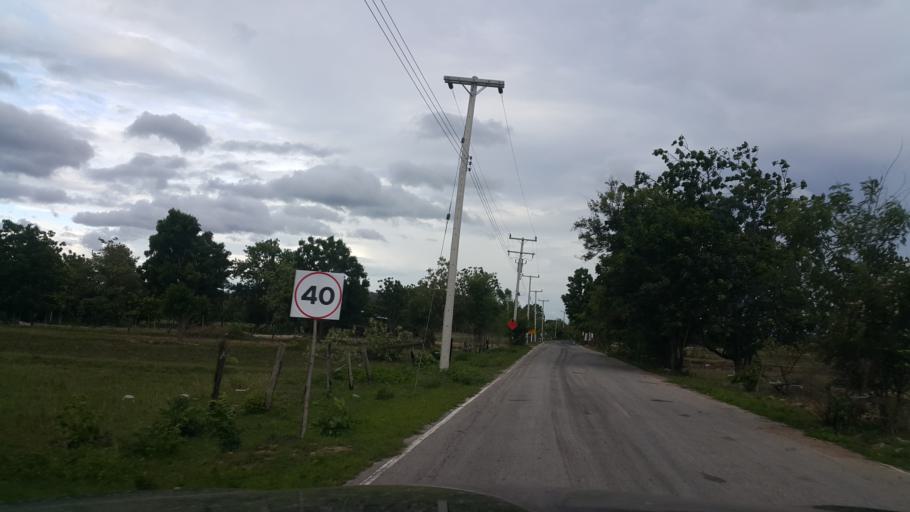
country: TH
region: Sukhothai
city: Thung Saliam
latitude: 17.1738
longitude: 99.4841
